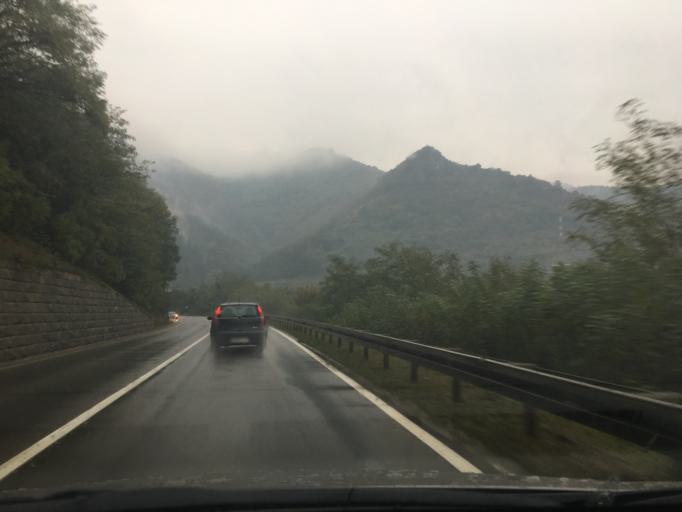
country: RS
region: Central Serbia
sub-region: Pcinjski Okrug
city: Vladicin Han
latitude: 42.7514
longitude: 22.0775
